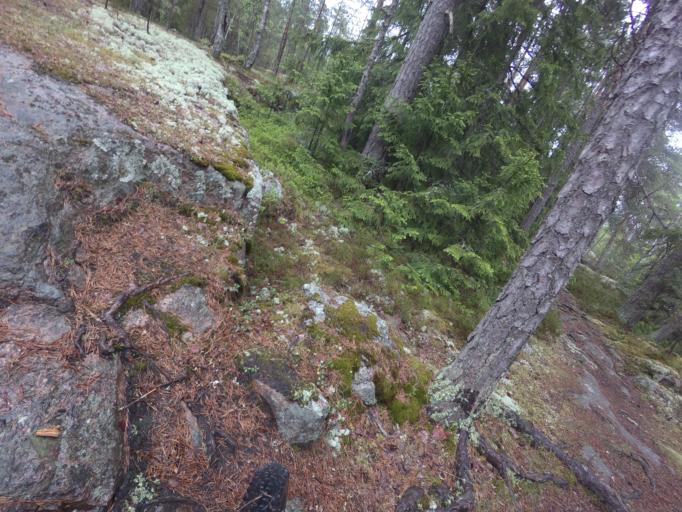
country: FI
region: Uusimaa
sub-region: Helsinki
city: Kauniainen
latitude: 60.1859
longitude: 24.7104
